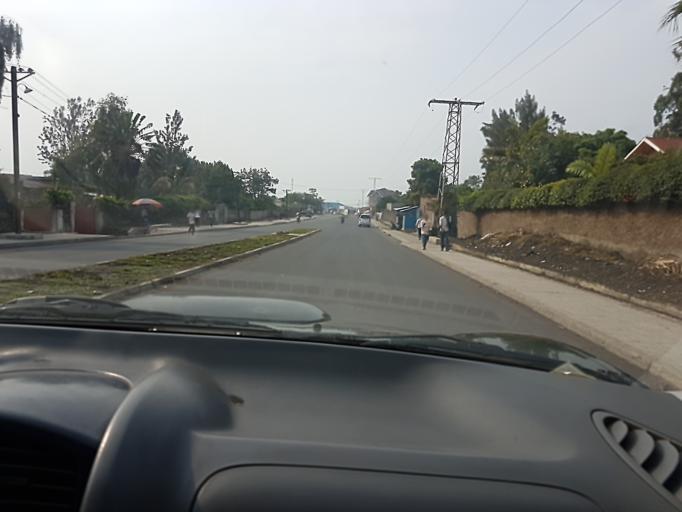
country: CD
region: Nord Kivu
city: Goma
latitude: -1.6838
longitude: 29.2285
